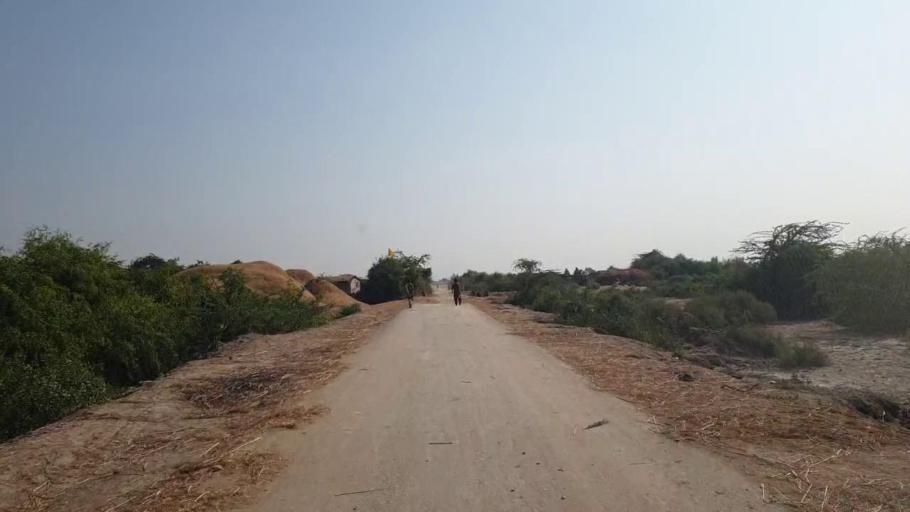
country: PK
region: Sindh
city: Matli
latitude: 24.9684
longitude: 68.6461
